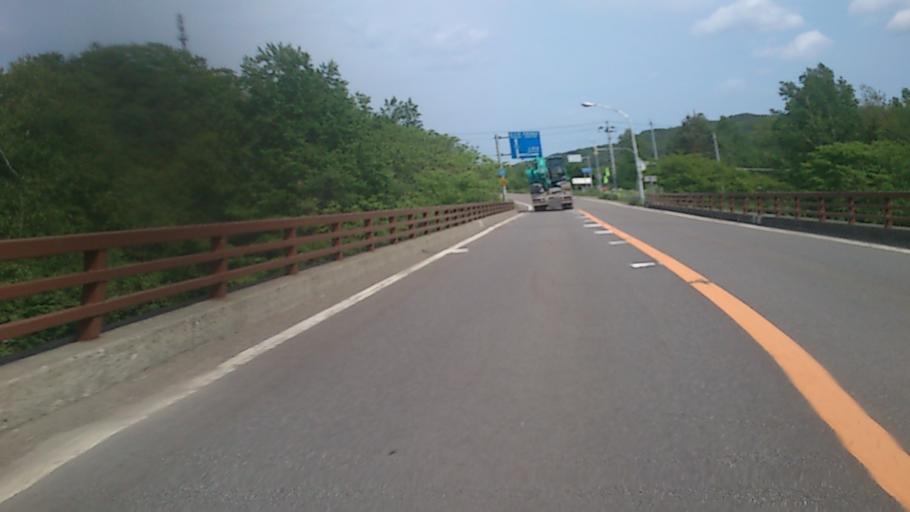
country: JP
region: Hokkaido
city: Kitami
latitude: 43.3086
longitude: 143.7055
